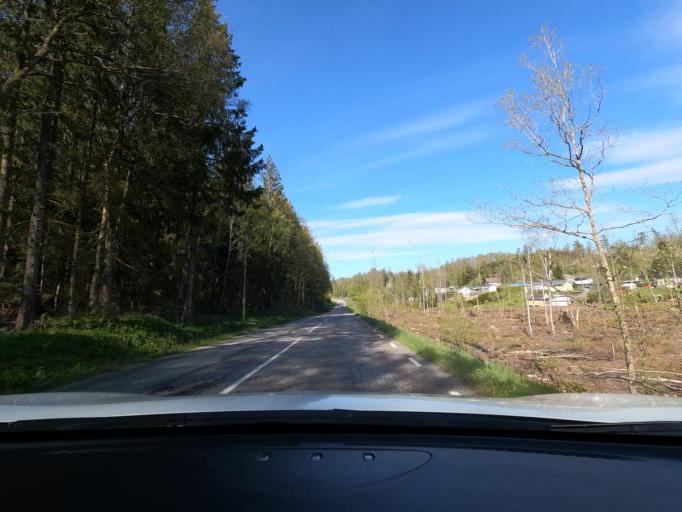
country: SE
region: Vaestra Goetaland
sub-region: Harryda Kommun
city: Landvetter
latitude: 57.6128
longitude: 12.2868
